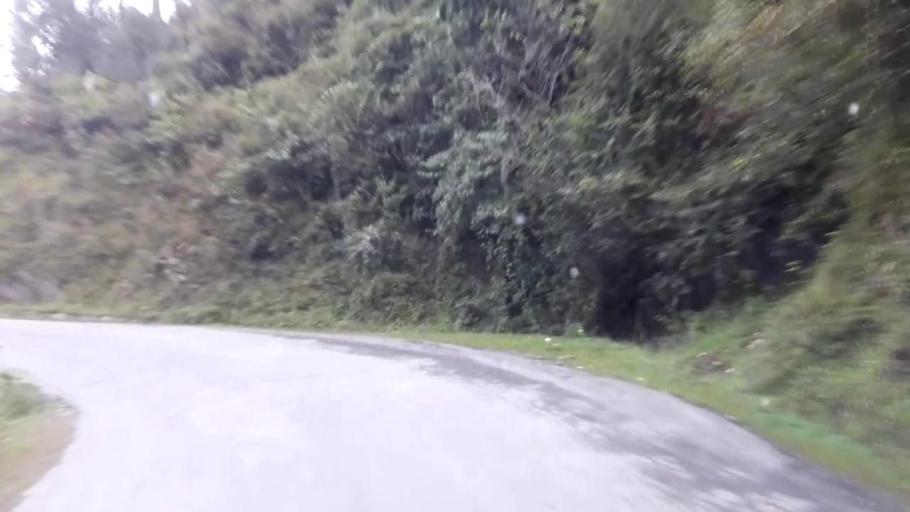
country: IN
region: Himachal Pradesh
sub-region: Shimla
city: Shimla
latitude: 31.0502
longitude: 77.1479
